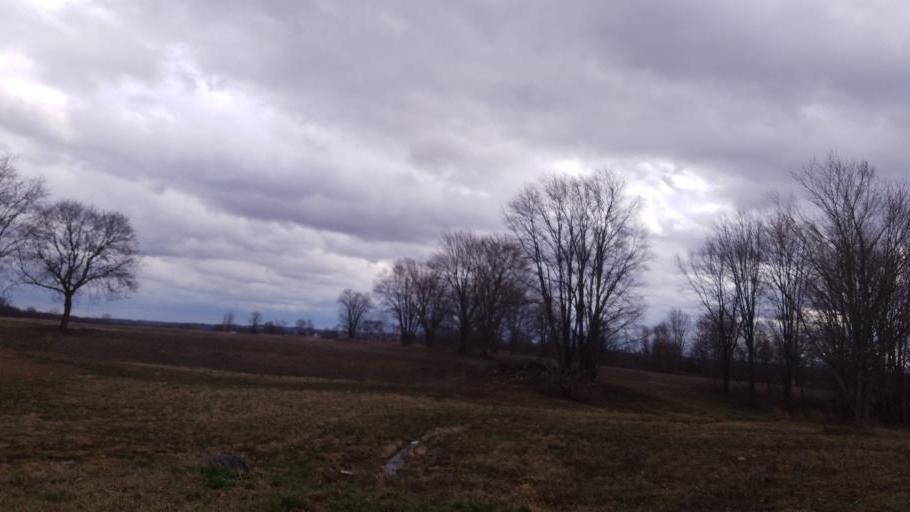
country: US
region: Ohio
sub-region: Licking County
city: Utica
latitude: 40.2923
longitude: -82.5132
